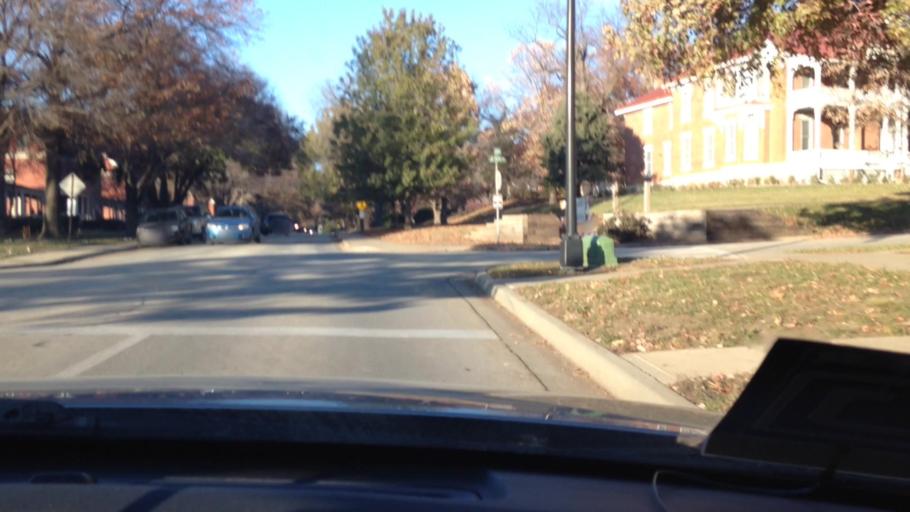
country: US
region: Kansas
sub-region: Leavenworth County
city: Leavenworth
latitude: 39.3522
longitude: -94.9179
